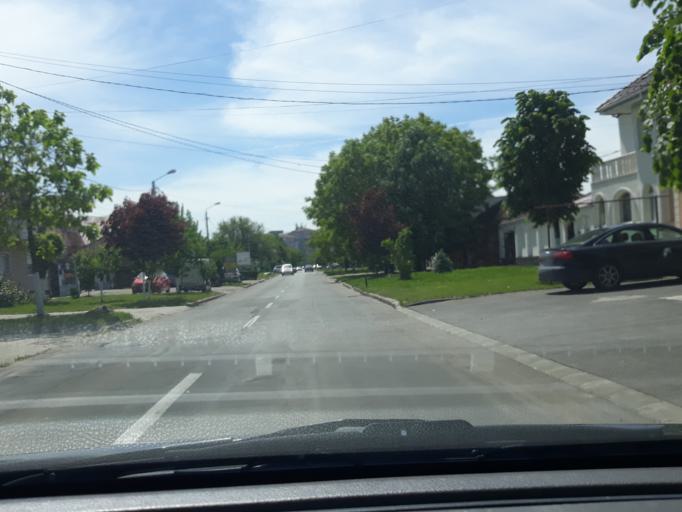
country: RO
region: Bihor
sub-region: Comuna Biharea
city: Oradea
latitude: 47.0589
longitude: 21.9061
